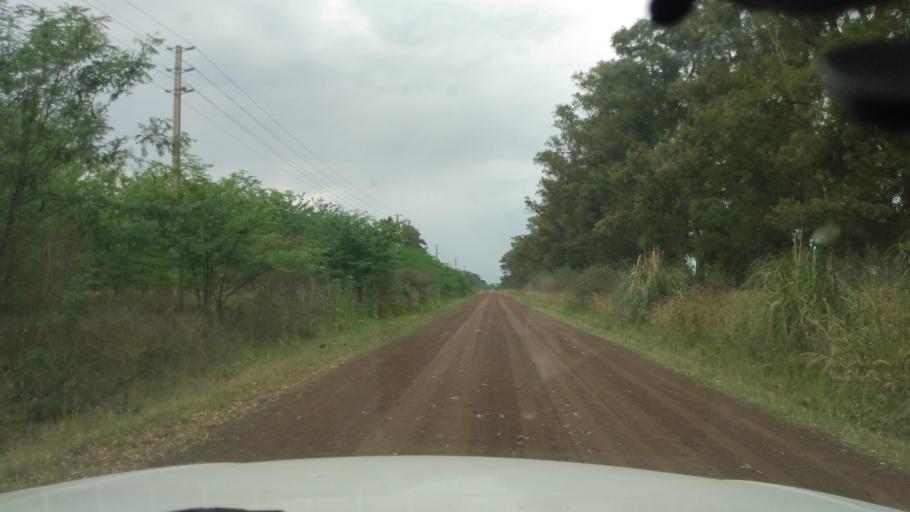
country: AR
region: Buenos Aires
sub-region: Partido de Lujan
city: Lujan
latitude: -34.5519
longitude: -59.1711
